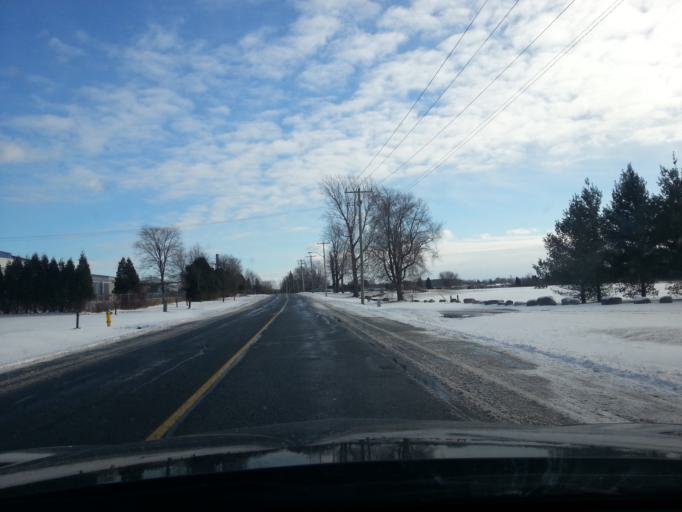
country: CA
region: Ontario
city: Cornwall
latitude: 45.0120
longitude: -74.7791
